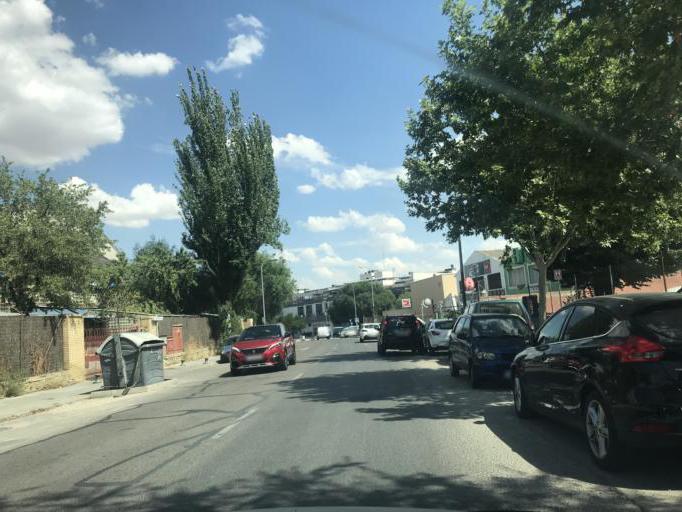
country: ES
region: Madrid
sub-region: Provincia de Madrid
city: Alcobendas
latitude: 40.5360
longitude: -3.6487
